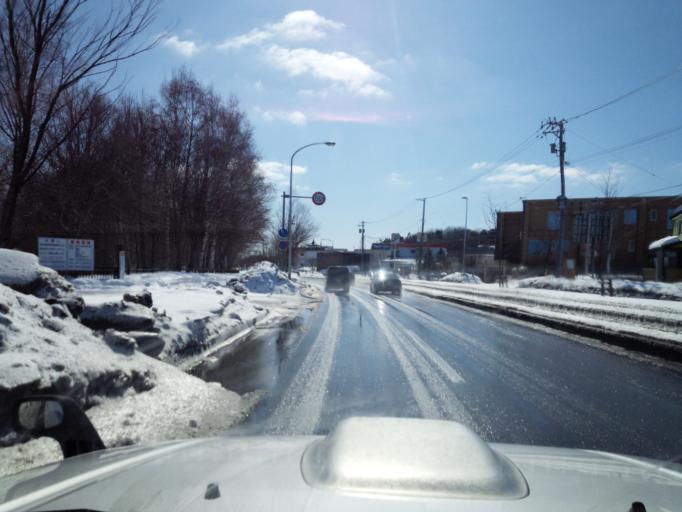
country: JP
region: Hokkaido
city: Kitahiroshima
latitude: 43.0034
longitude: 141.4600
